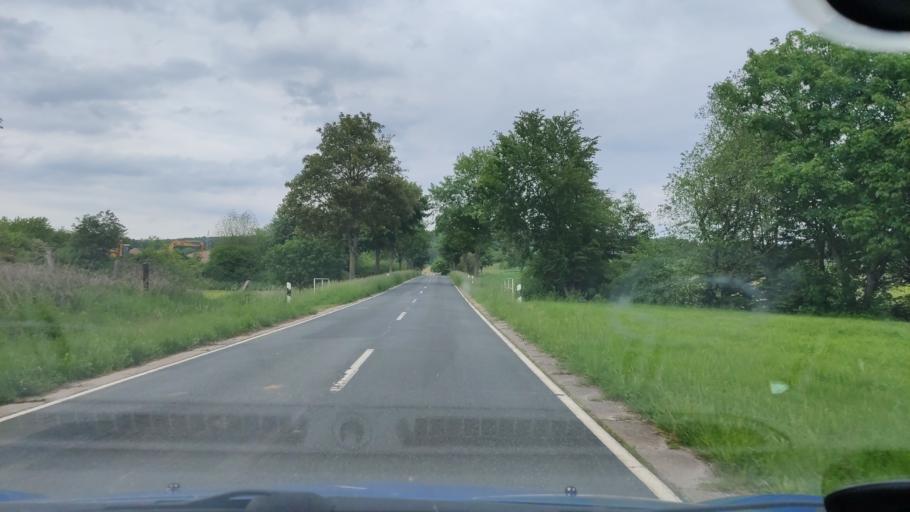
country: DE
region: Lower Saxony
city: Freden
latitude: 51.8949
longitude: 9.8685
